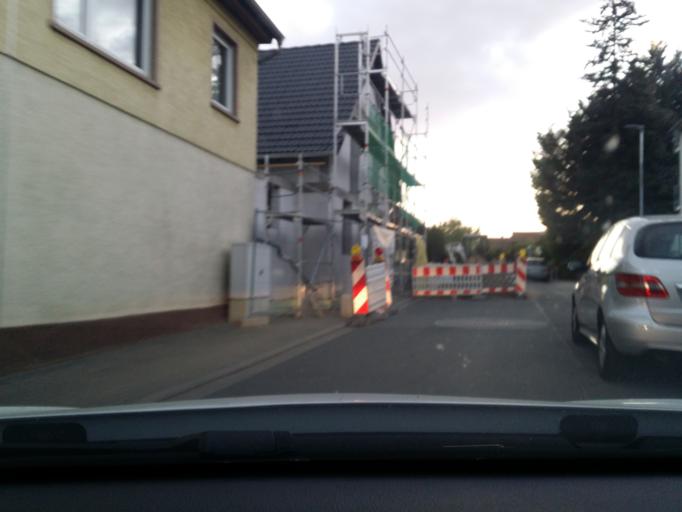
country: DE
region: Hesse
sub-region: Regierungsbezirk Darmstadt
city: Bickenbach
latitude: 49.7582
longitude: 8.6124
